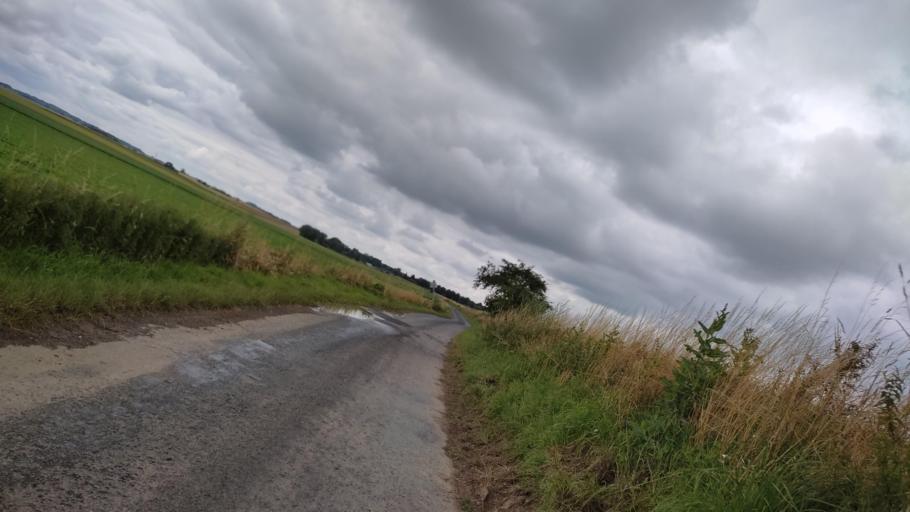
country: FR
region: Nord-Pas-de-Calais
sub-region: Departement du Pas-de-Calais
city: Dainville
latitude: 50.2711
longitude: 2.6979
